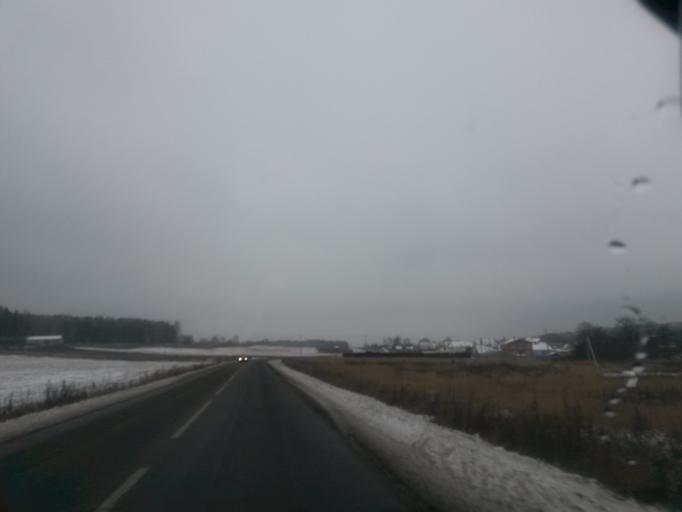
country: RU
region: Moskovskaya
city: Lyubuchany
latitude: 55.2838
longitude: 37.6211
